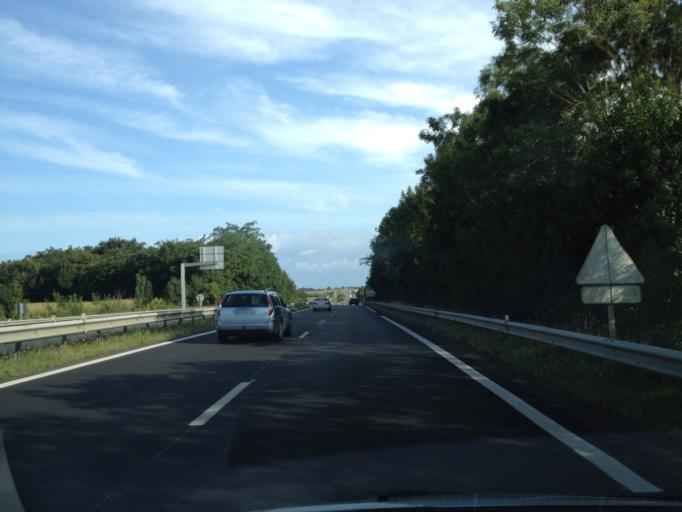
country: FR
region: Poitou-Charentes
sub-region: Departement de la Charente-Maritime
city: Saint-Laurent-de-la-Pree
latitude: 45.9932
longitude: -1.0387
